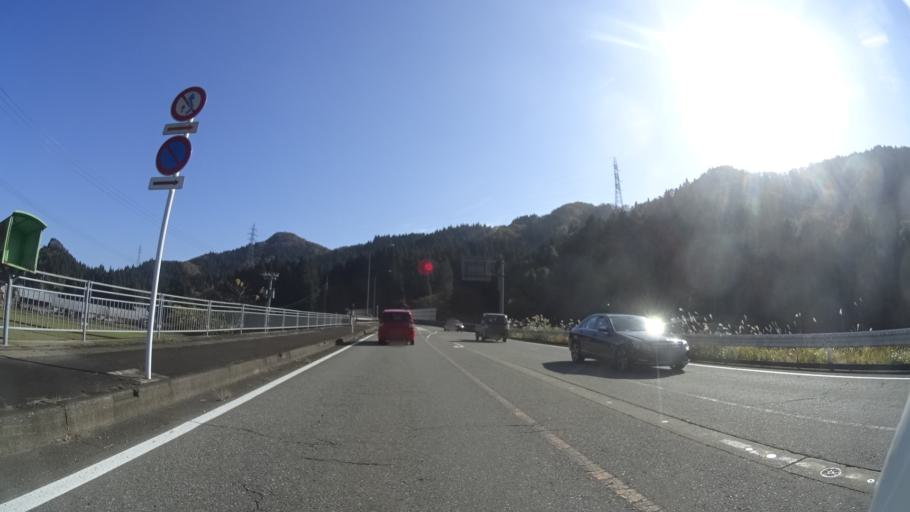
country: JP
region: Fukui
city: Ono
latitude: 35.9980
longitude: 136.4282
